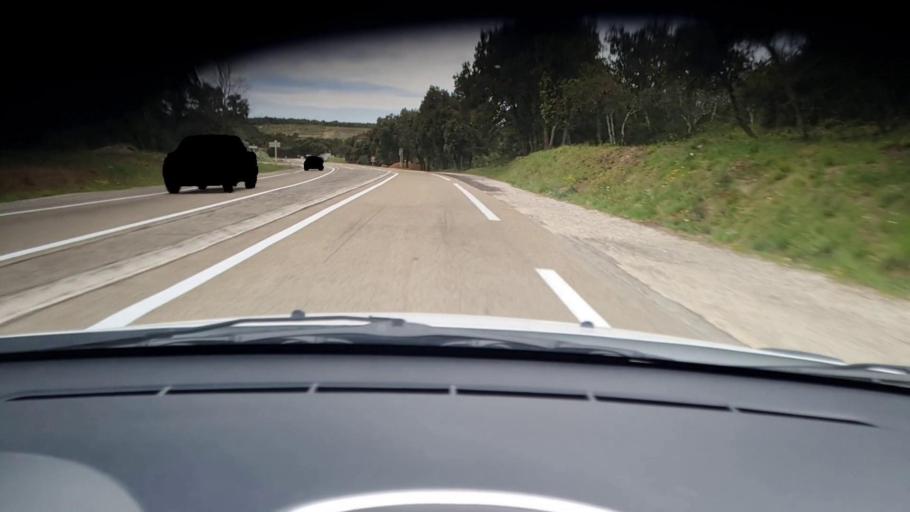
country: FR
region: Languedoc-Roussillon
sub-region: Departement du Gard
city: Poulx
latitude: 43.9190
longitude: 4.3889
